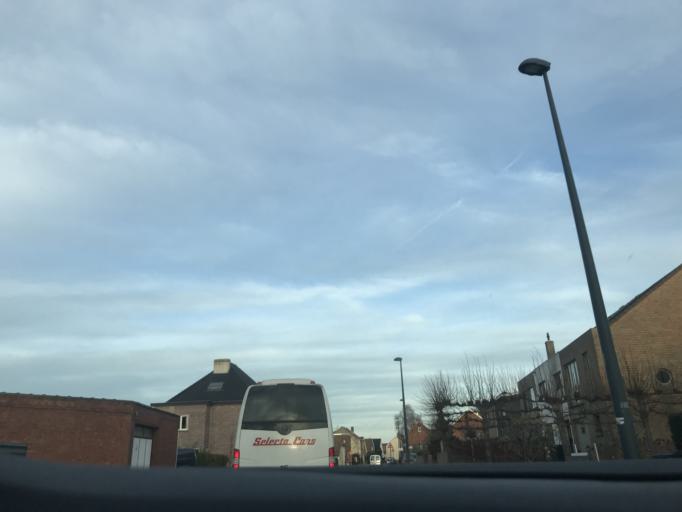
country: BE
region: Flanders
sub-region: Provincie Oost-Vlaanderen
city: Destelbergen
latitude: 51.0924
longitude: 3.7587
